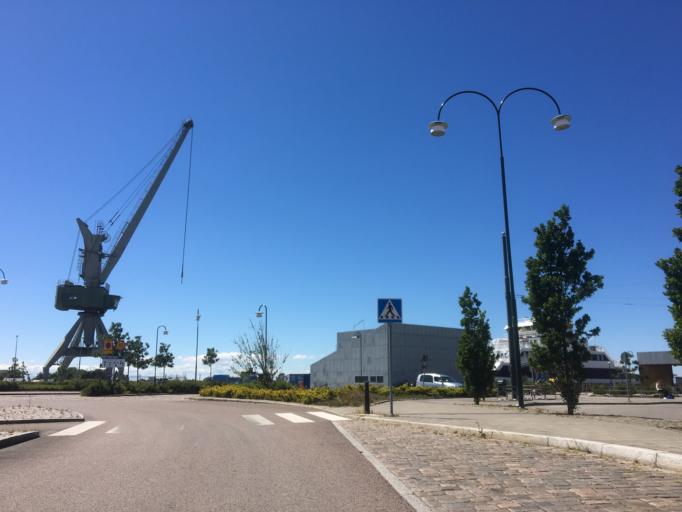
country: SE
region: Skane
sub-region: Landskrona
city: Landskrona
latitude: 55.8657
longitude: 12.8271
